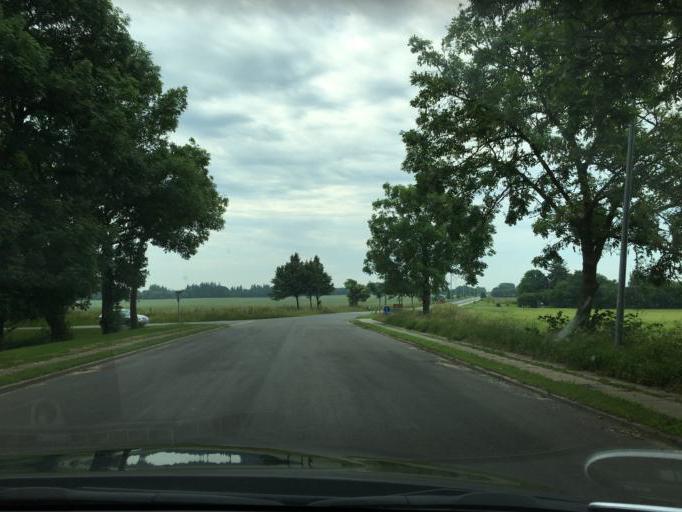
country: DK
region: South Denmark
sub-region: Kolding Kommune
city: Kolding
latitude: 55.5816
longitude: 9.4925
